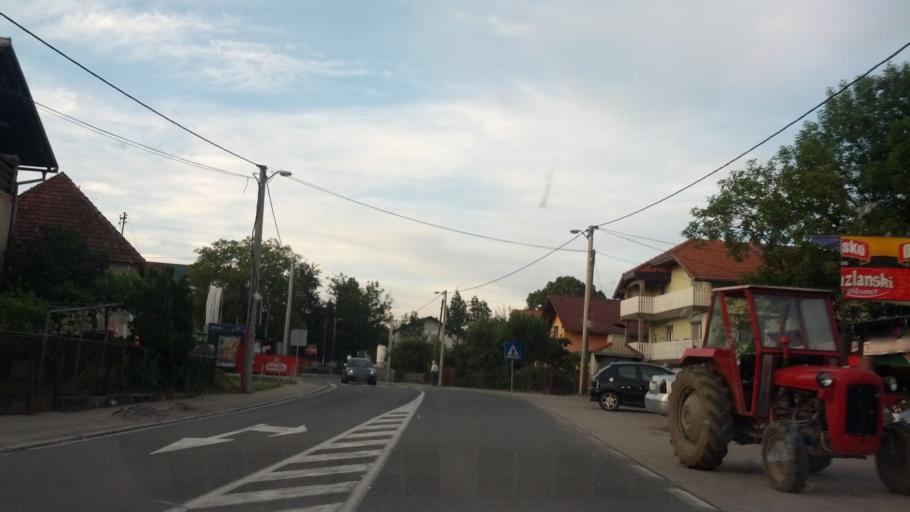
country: BA
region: Federation of Bosnia and Herzegovina
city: Izacic
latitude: 44.8784
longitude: 15.7758
